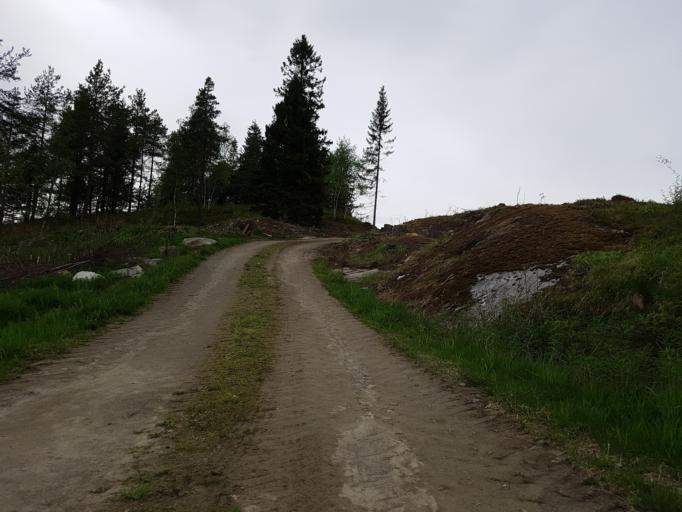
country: NO
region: Nord-Trondelag
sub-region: Levanger
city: Skogn
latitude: 63.6309
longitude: 11.2577
